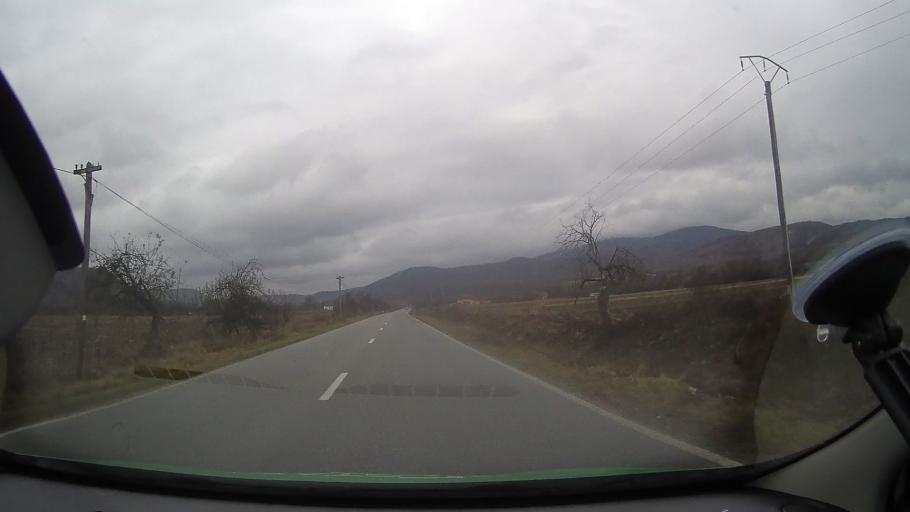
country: RO
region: Arad
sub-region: Comuna Buteni
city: Buteni
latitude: 46.3150
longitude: 22.1384
